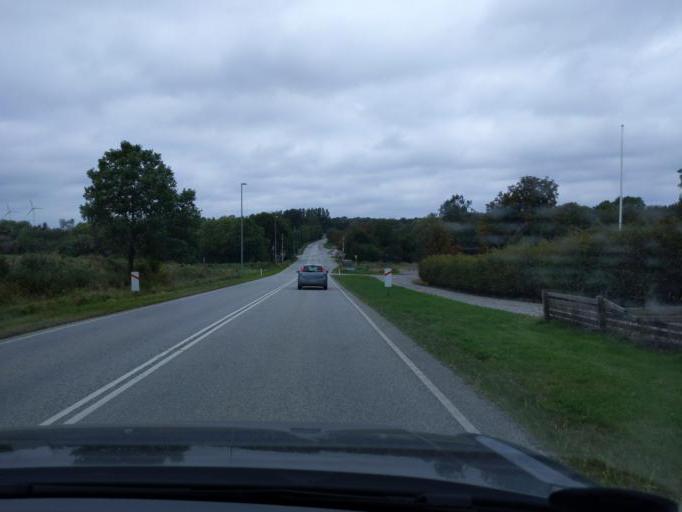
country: DK
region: North Denmark
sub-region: Mariagerfjord Kommune
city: Hobro
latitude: 56.5682
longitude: 9.8250
